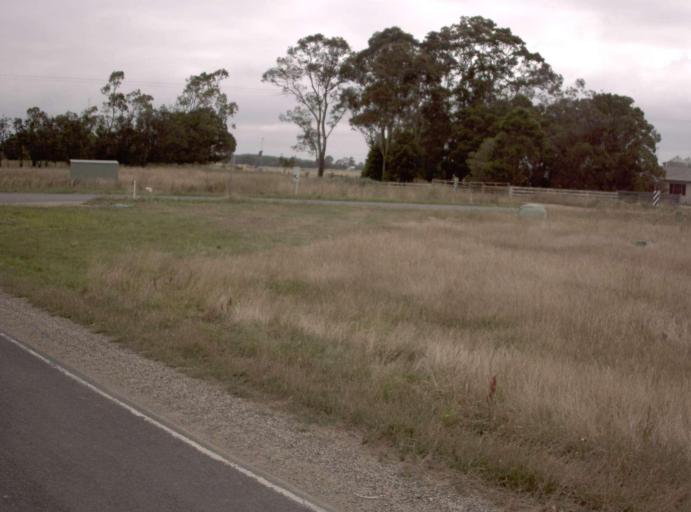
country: AU
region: Victoria
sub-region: Wellington
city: Heyfield
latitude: -38.0320
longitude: 146.7661
